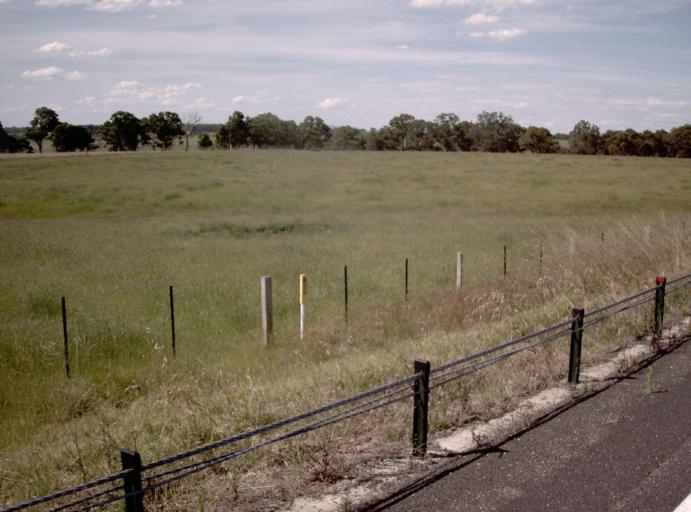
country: AU
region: Victoria
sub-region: East Gippsland
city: Lakes Entrance
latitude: -37.8208
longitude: 147.8092
